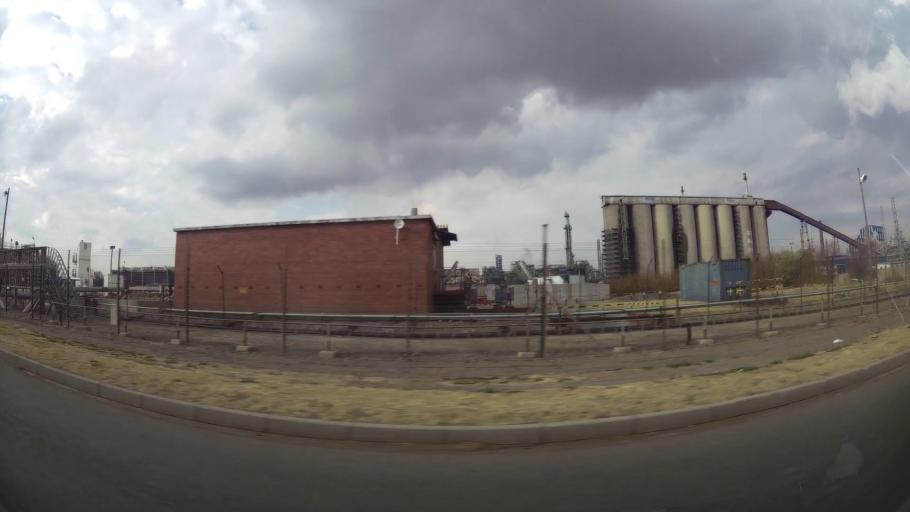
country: ZA
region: Orange Free State
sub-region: Fezile Dabi District Municipality
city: Sasolburg
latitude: -26.8245
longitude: 27.8369
